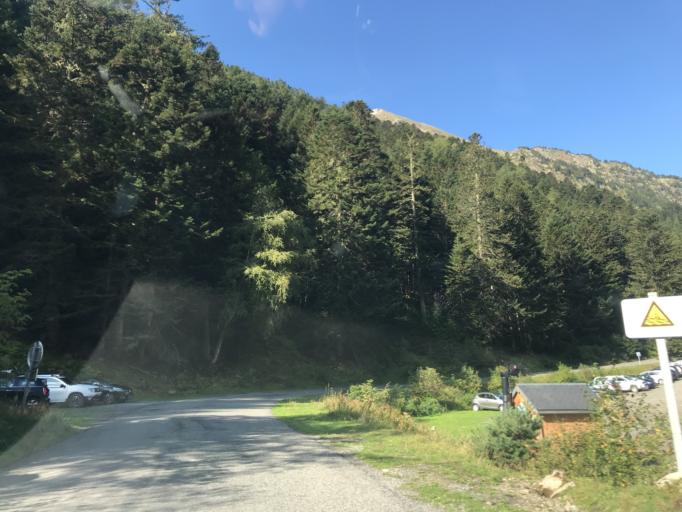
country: FR
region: Midi-Pyrenees
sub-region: Departement des Hautes-Pyrenees
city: Saint-Lary-Soulan
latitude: 42.8190
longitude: 0.1912
